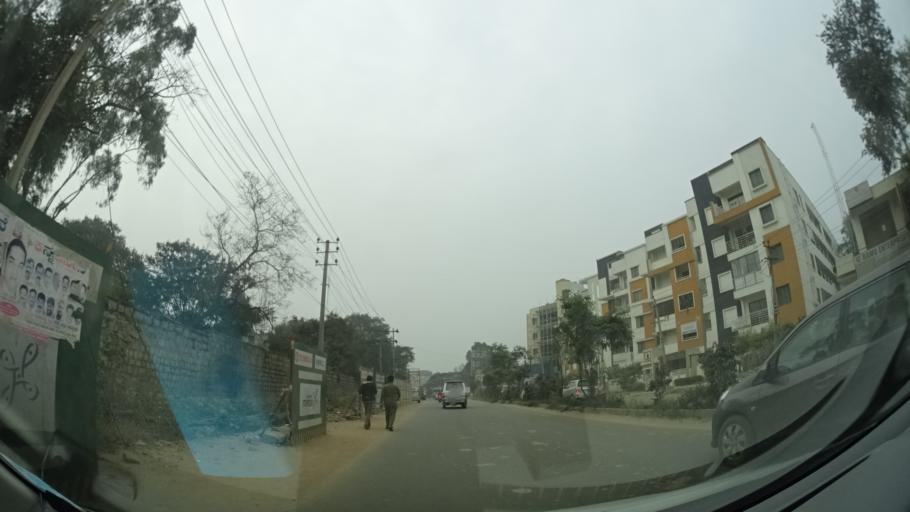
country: IN
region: Karnataka
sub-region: Bangalore Urban
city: Bangalore
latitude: 12.9865
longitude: 77.7088
